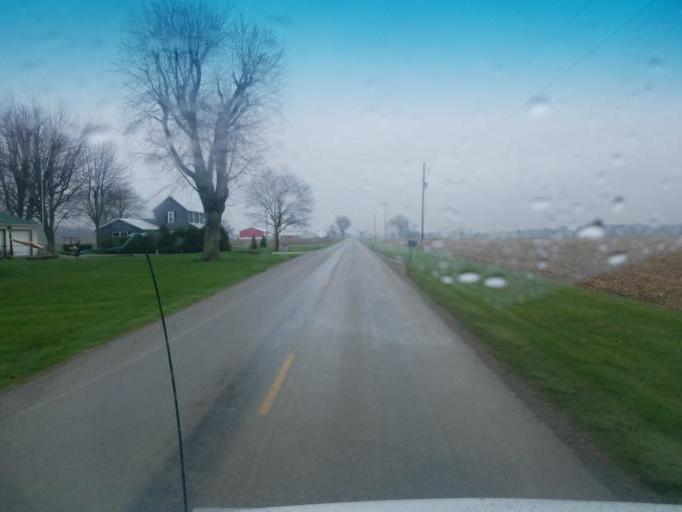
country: US
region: Ohio
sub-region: Wyandot County
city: Carey
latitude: 40.9854
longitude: -83.2880
